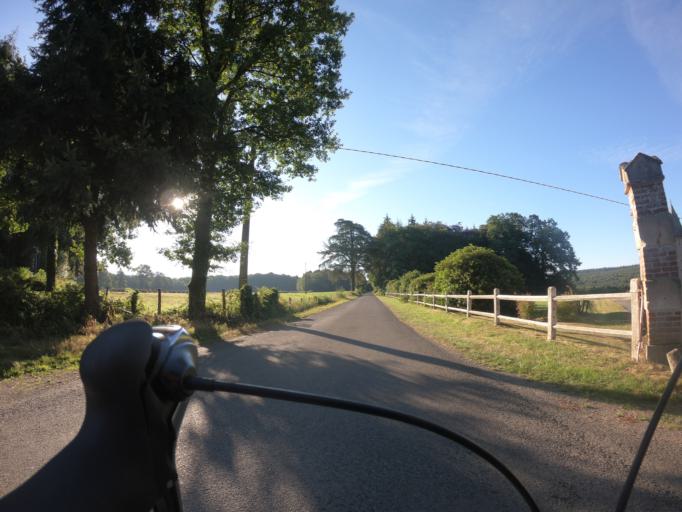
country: FR
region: Lower Normandy
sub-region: Departement de l'Orne
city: Magny-le-Desert
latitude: 48.5348
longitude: -0.2782
